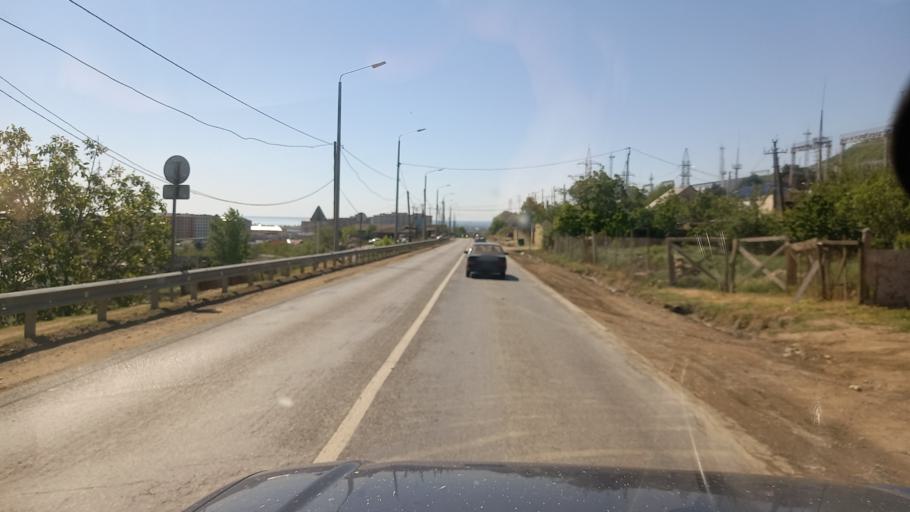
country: RU
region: Dagestan
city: Derbent
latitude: 42.0438
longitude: 48.2876
